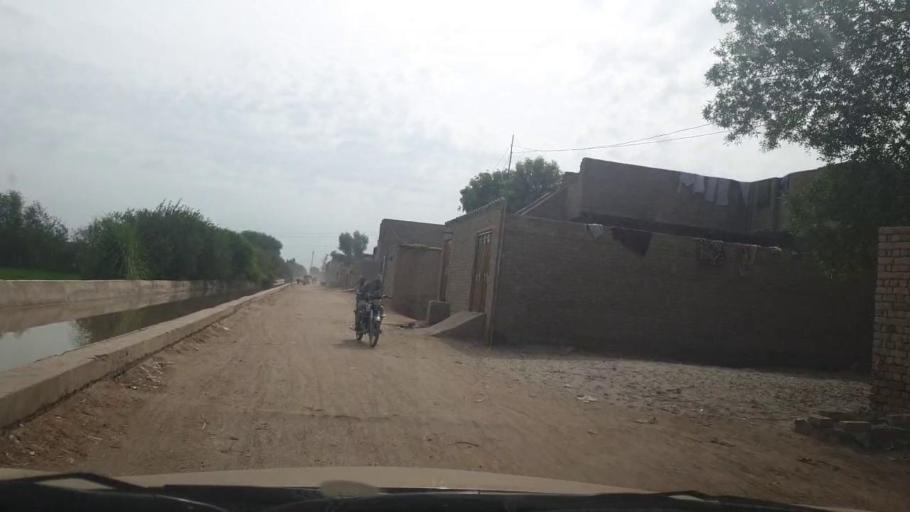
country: PK
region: Sindh
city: Larkana
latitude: 27.5814
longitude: 68.2099
